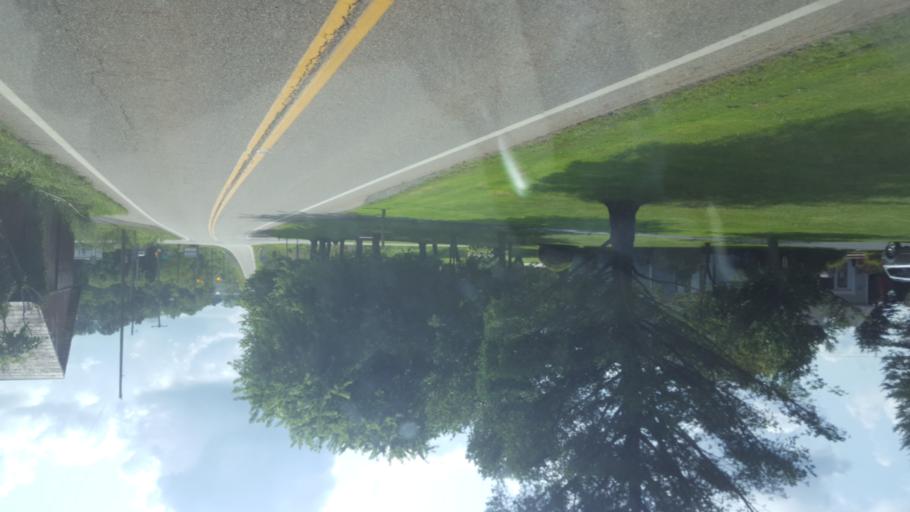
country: US
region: Ohio
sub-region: Columbiana County
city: Lisbon
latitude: 40.7891
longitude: -80.8597
